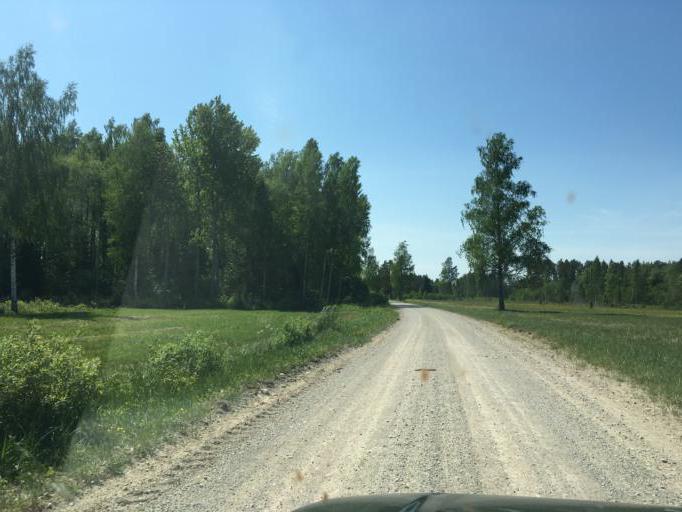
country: LV
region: Rojas
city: Roja
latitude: 57.4268
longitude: 22.7172
